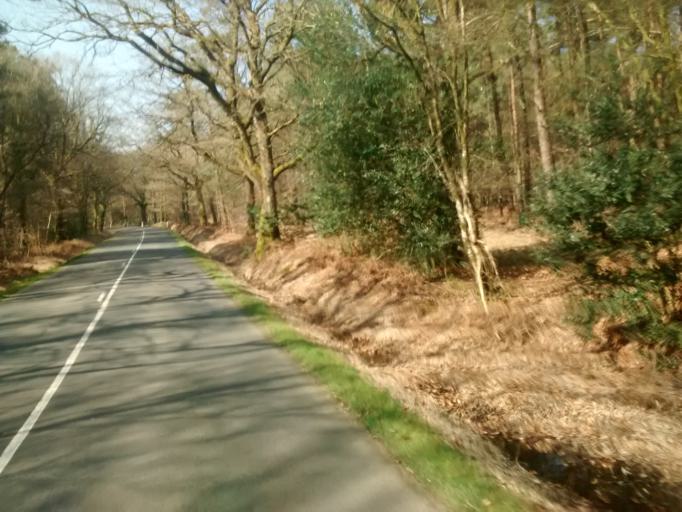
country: FR
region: Brittany
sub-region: Departement d'Ille-et-Vilaine
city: Paimpont
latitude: 48.0132
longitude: -2.1362
